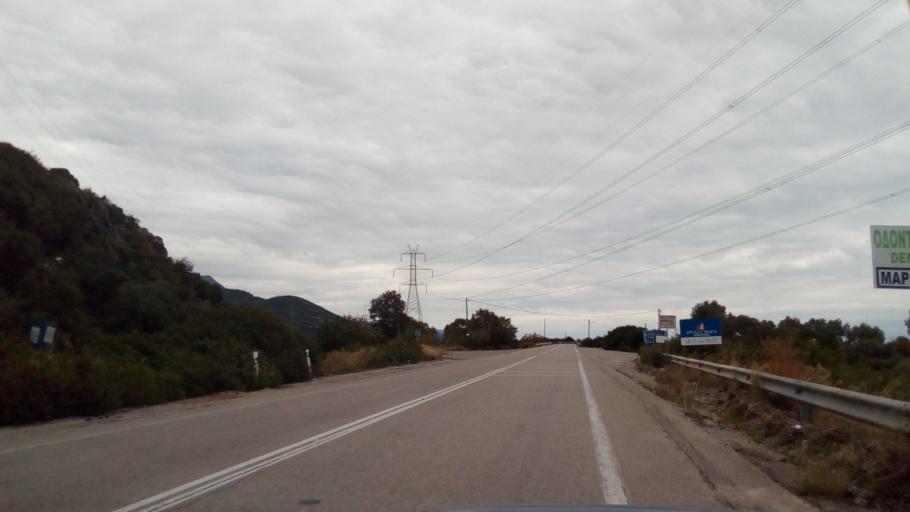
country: GR
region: West Greece
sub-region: Nomos Achaias
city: Kamarai
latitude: 38.3988
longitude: 22.0027
